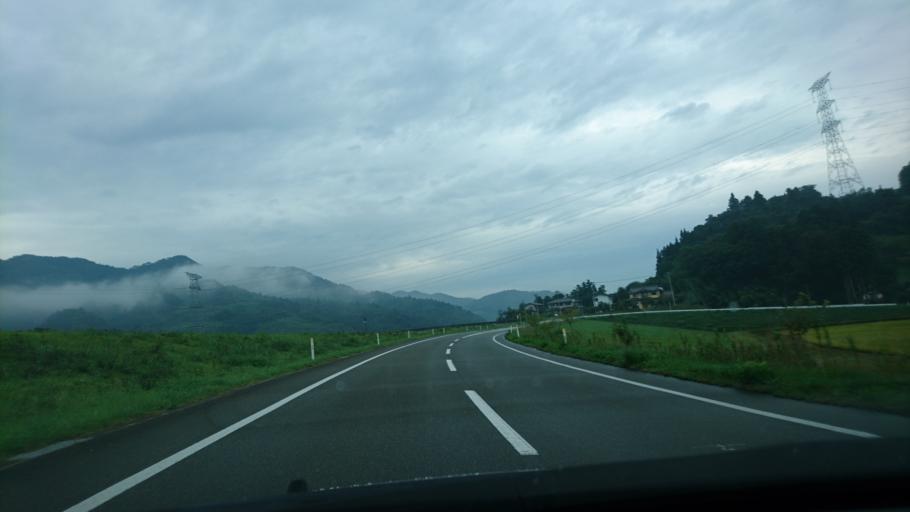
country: JP
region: Iwate
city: Ichinoseki
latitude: 38.9330
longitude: 141.2502
